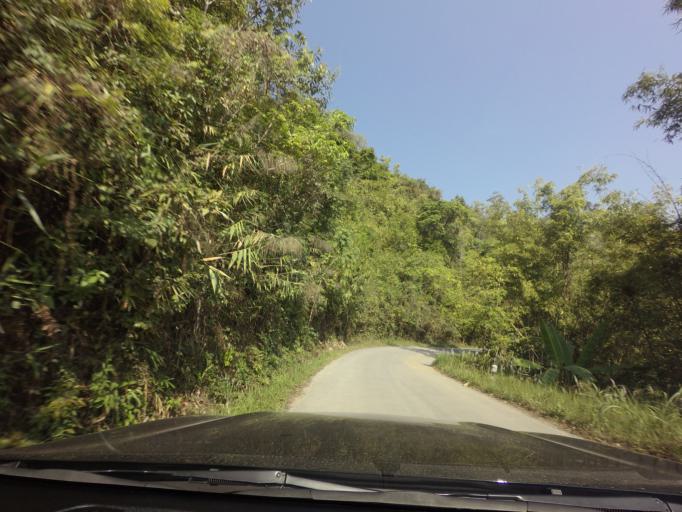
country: TH
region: Kanchanaburi
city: Thong Pha Phum
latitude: 14.6929
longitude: 98.4572
